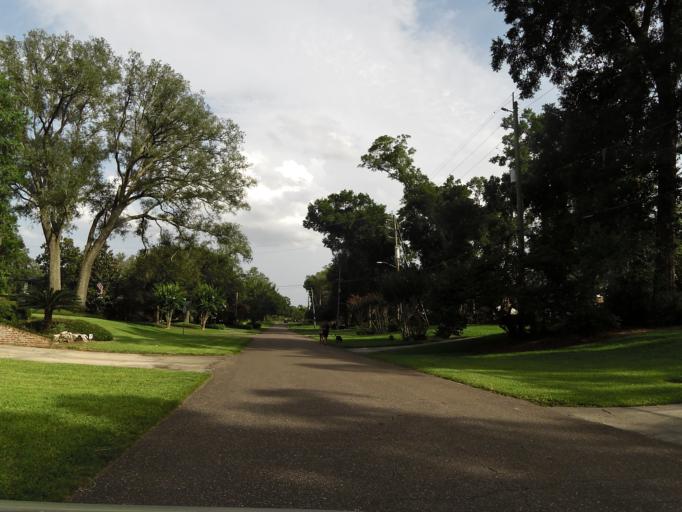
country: US
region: Florida
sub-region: Clay County
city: Bellair-Meadowbrook Terrace
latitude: 30.2620
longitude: -81.7123
